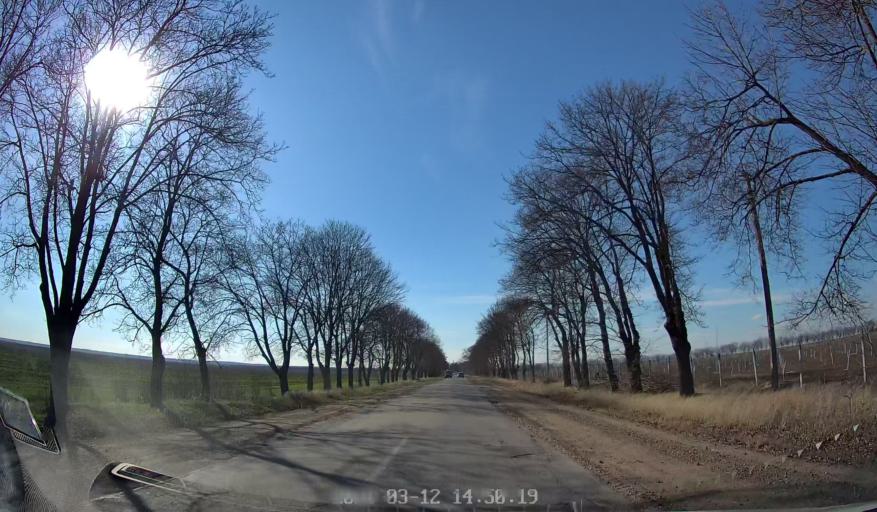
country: MD
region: Criuleni
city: Criuleni
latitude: 47.2229
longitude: 29.1321
